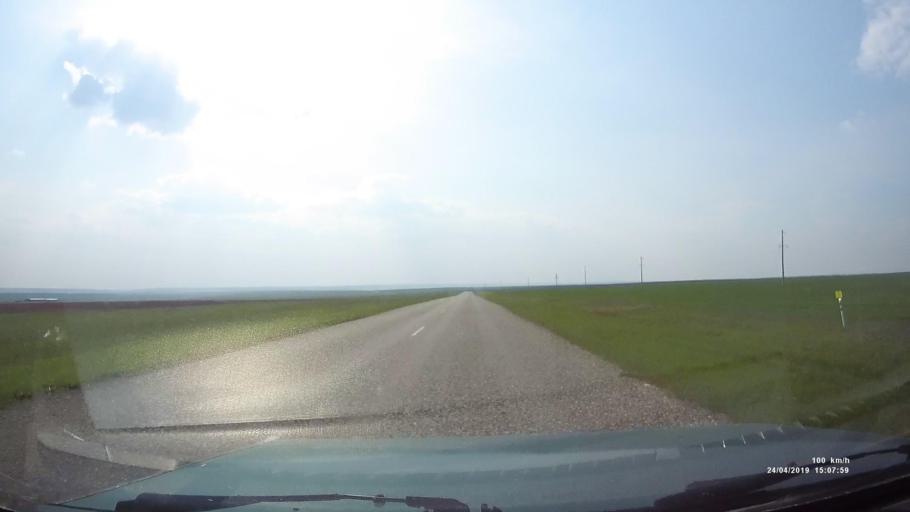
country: RU
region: Rostov
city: Remontnoye
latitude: 46.5599
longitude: 43.3928
